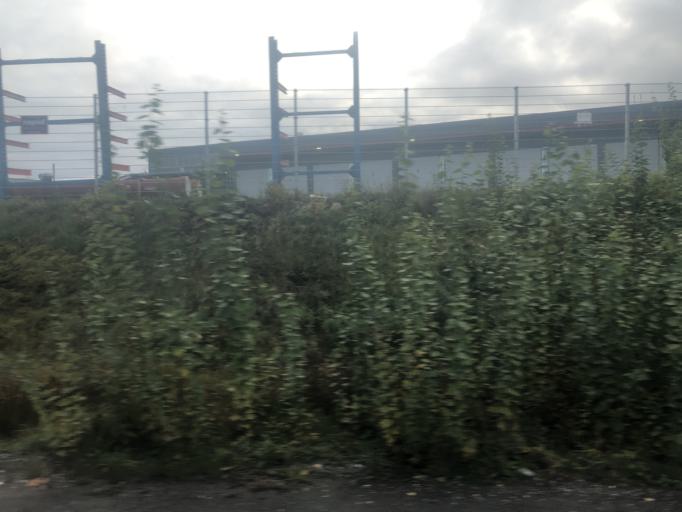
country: SE
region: Stockholm
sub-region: Jarfalla Kommun
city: Jakobsberg
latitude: 59.4108
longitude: 17.8373
